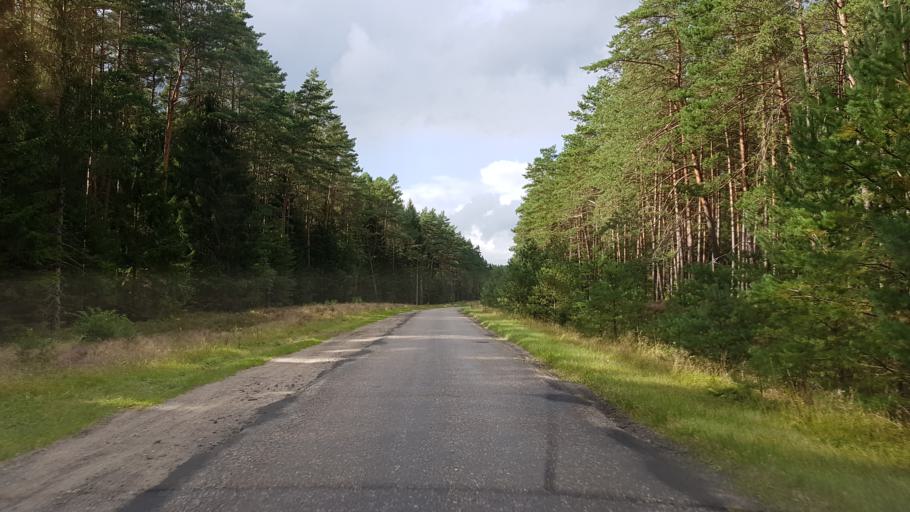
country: PL
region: West Pomeranian Voivodeship
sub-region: Powiat bialogardzki
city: Tychowo
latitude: 54.0440
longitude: 16.3173
